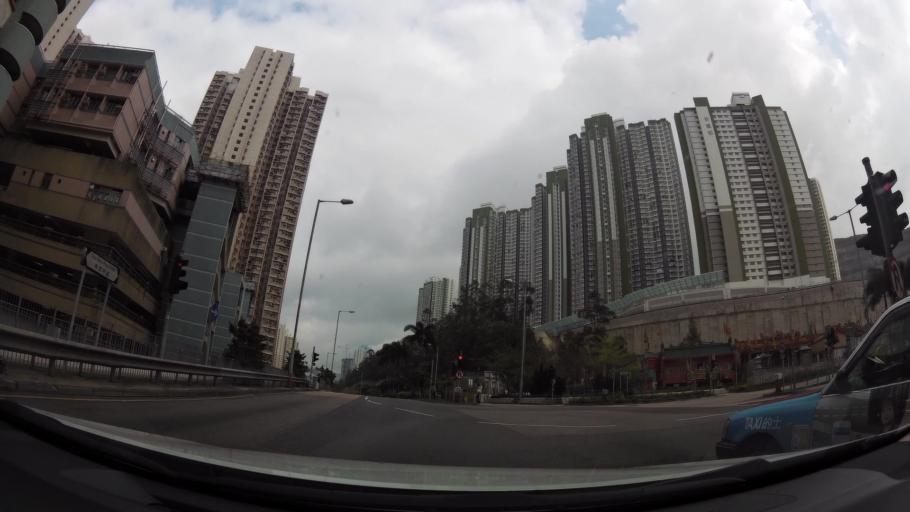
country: HK
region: Kowloon City
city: Kowloon
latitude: 22.3178
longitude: 114.2354
